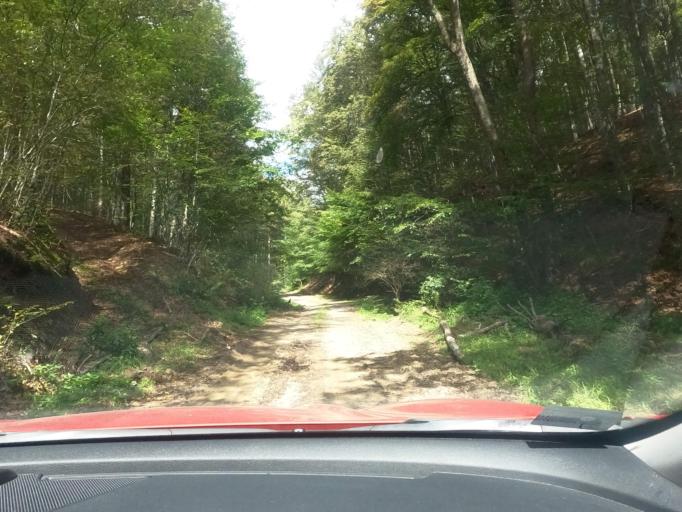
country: BA
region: Federation of Bosnia and Herzegovina
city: Velika Kladusa
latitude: 45.2413
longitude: 15.7738
